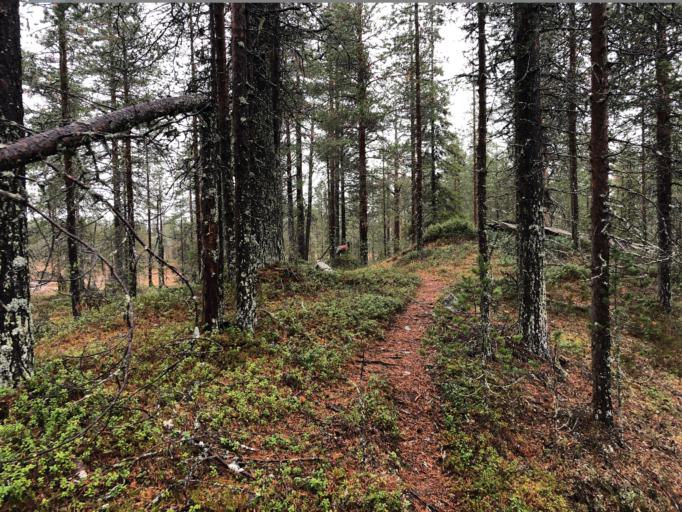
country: FI
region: Lapland
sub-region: Itae-Lappi
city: Posio
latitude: 65.9921
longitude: 28.5463
